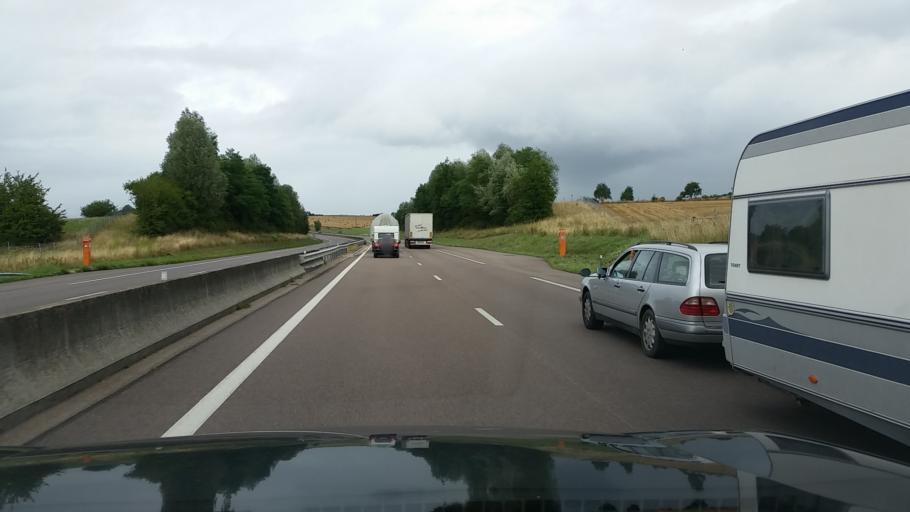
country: FR
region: Lorraine
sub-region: Departement des Vosges
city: Chatenois
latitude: 48.3712
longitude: 5.8744
